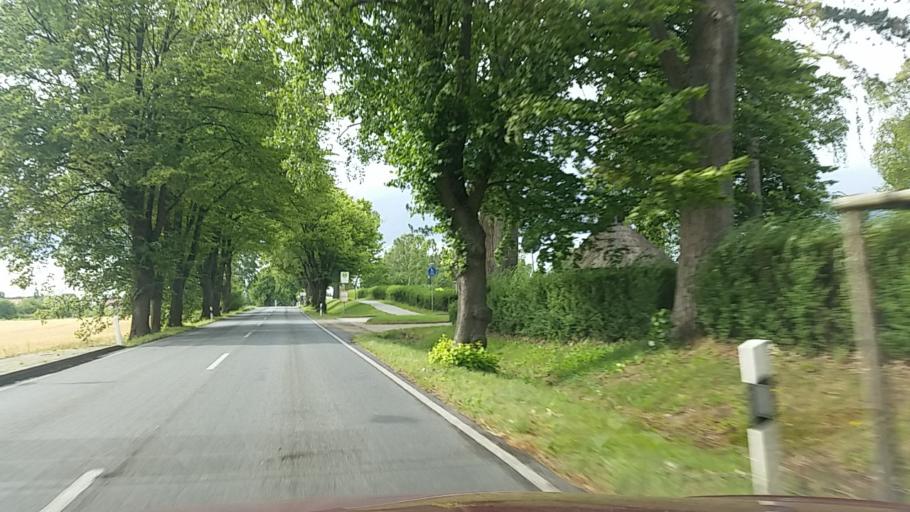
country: DE
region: Mecklenburg-Vorpommern
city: Ostseebad Kuhlungsborn
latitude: 54.1417
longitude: 11.7721
